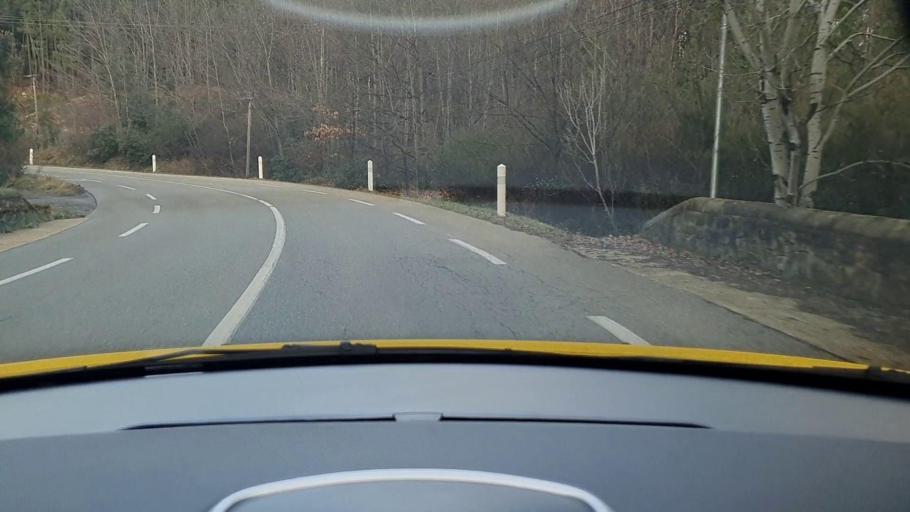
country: FR
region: Languedoc-Roussillon
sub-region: Departement du Gard
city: Les Salles-du-Gardon
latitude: 44.2591
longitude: 4.0453
